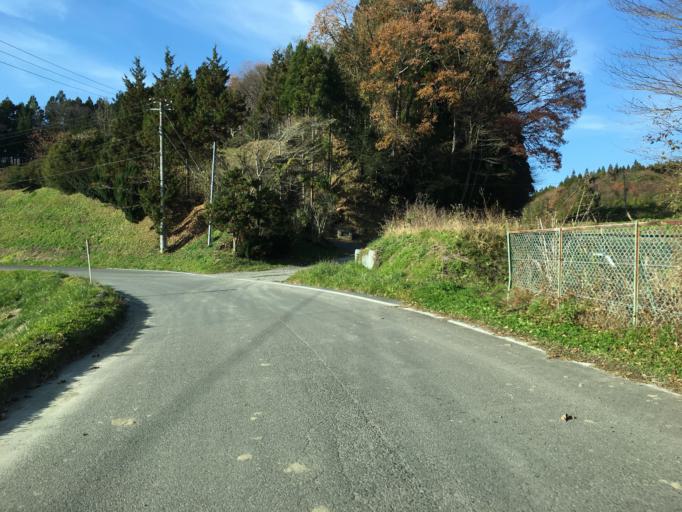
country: JP
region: Fukushima
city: Ishikawa
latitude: 37.2478
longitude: 140.5831
